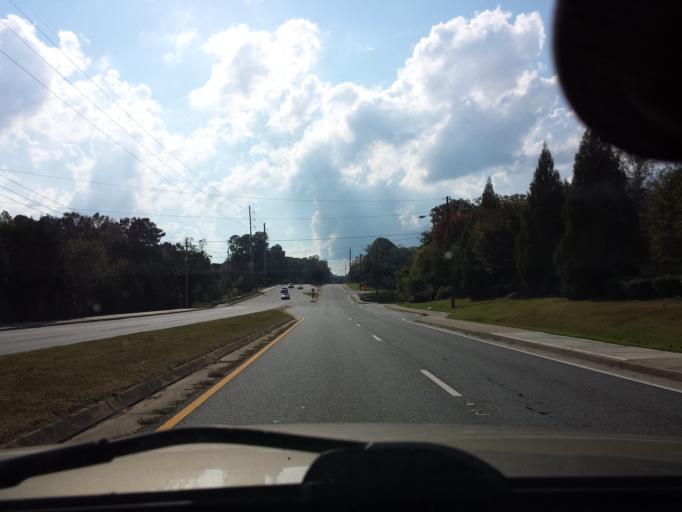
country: US
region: Georgia
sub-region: Cobb County
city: Marietta
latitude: 33.9774
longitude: -84.4672
